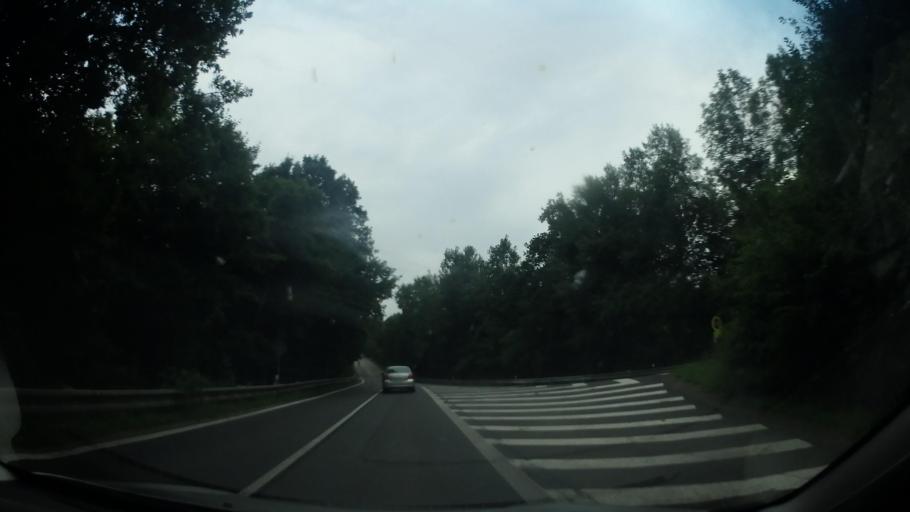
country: CZ
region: South Moravian
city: Troubsko
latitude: 49.1989
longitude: 16.5173
